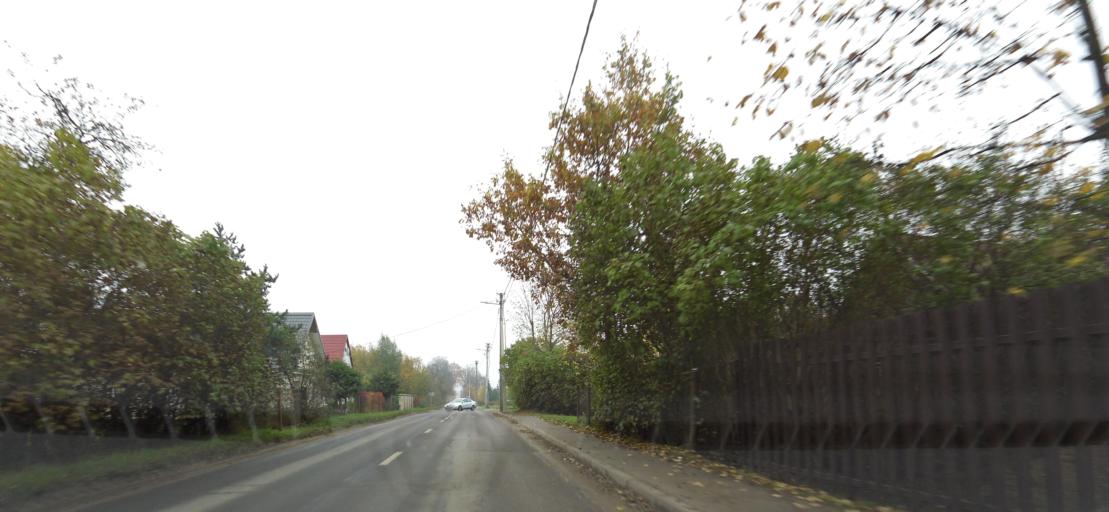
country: LT
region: Vilnius County
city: Rasos
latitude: 54.6621
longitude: 25.3451
